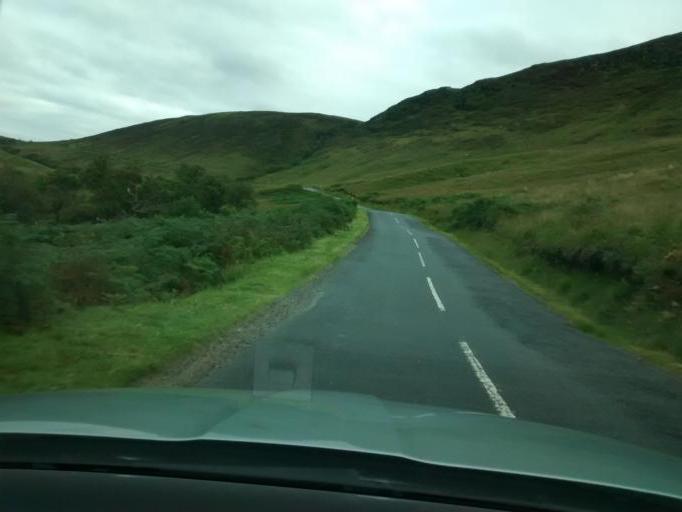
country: GB
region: Scotland
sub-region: North Ayrshire
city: Isle of Arran
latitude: 55.6973
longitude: -5.2540
